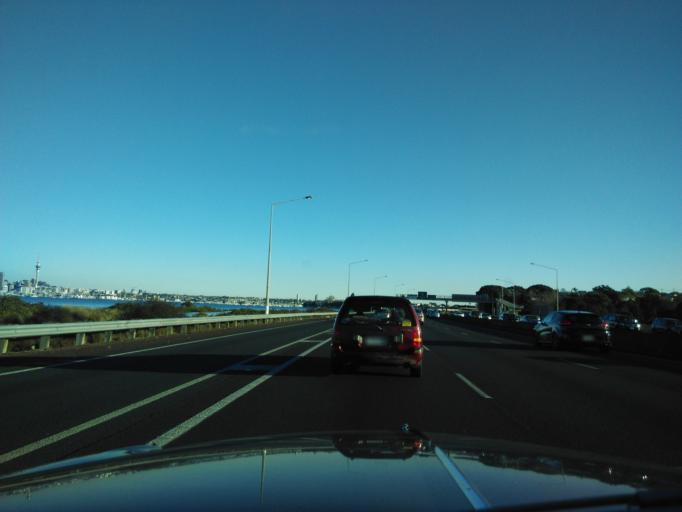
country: NZ
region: Auckland
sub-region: Auckland
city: North Shore
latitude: -36.8055
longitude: 174.7598
